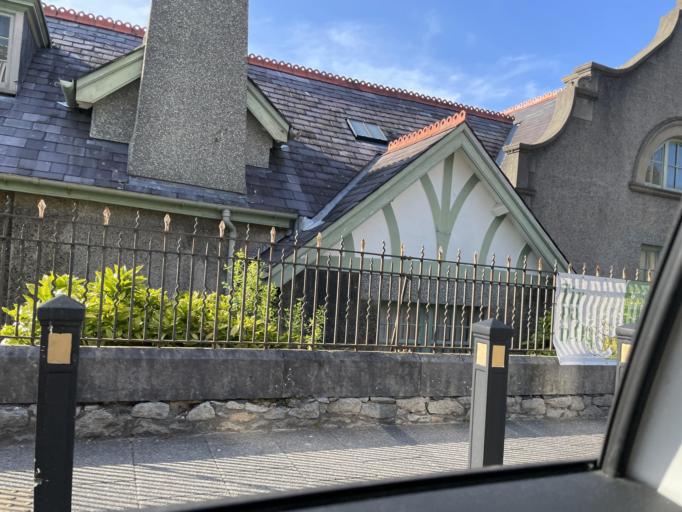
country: GB
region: Wales
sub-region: Gwynedd
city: Bangor
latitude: 53.2295
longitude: -4.1309
